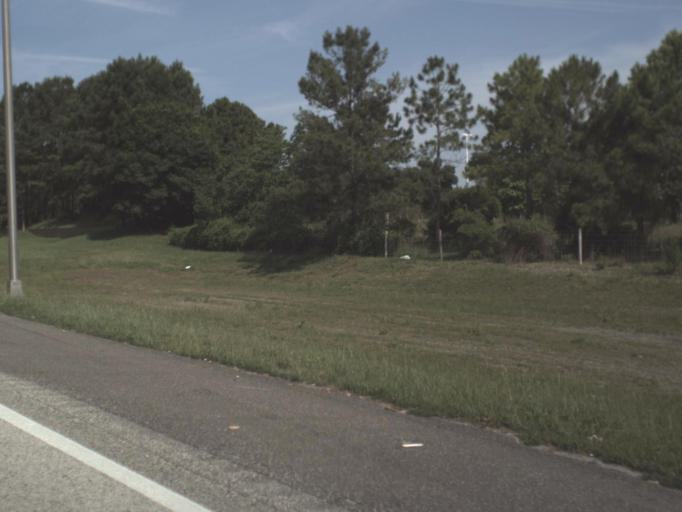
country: US
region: Florida
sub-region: Duval County
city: Jacksonville
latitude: 30.2501
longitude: -81.5467
